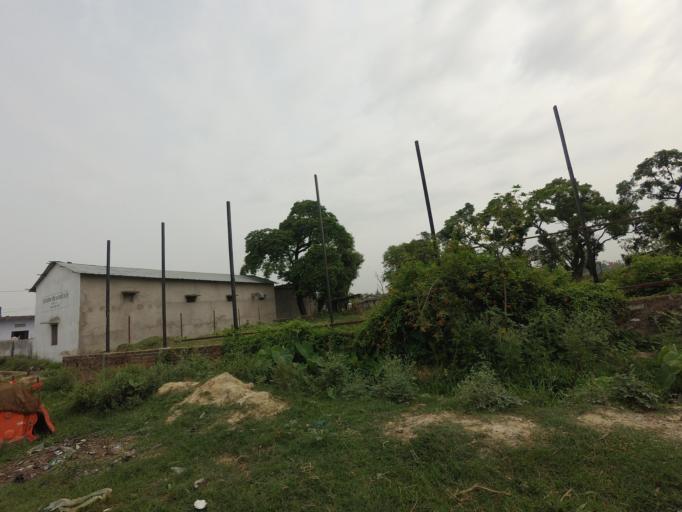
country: NP
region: Western Region
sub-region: Lumbini Zone
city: Bhairahawa
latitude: 27.4844
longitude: 83.4254
